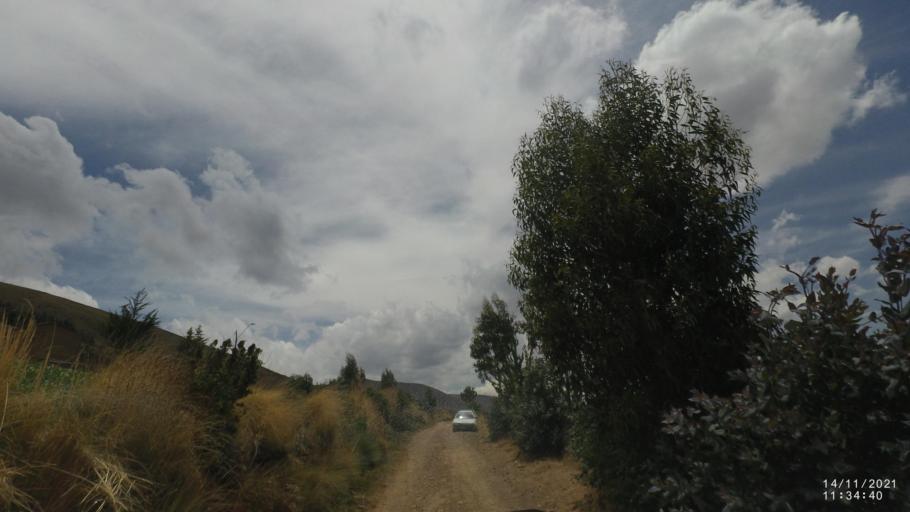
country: BO
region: Cochabamba
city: Colomi
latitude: -17.3449
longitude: -66.0040
